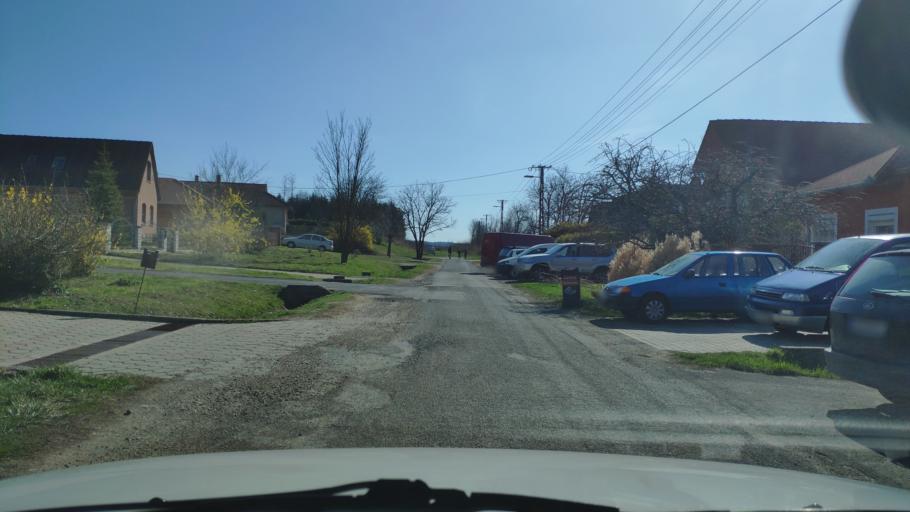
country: HU
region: Zala
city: Nagykanizsa
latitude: 46.4068
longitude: 16.9806
